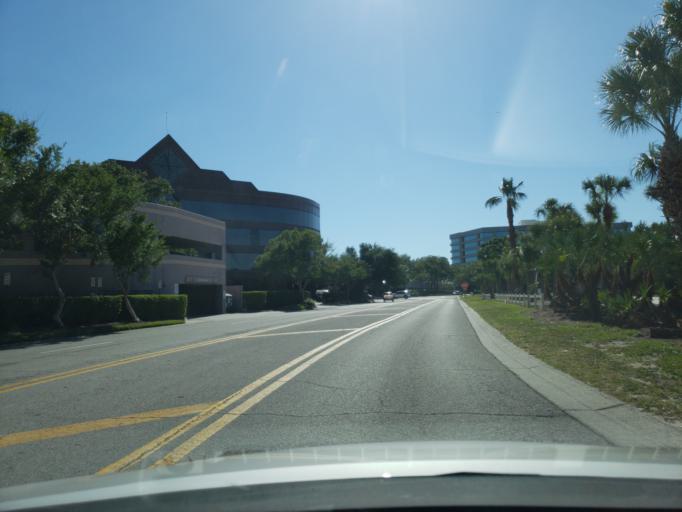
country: US
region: Florida
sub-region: Hillsborough County
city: Town 'n' Country
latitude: 27.9684
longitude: -82.5667
